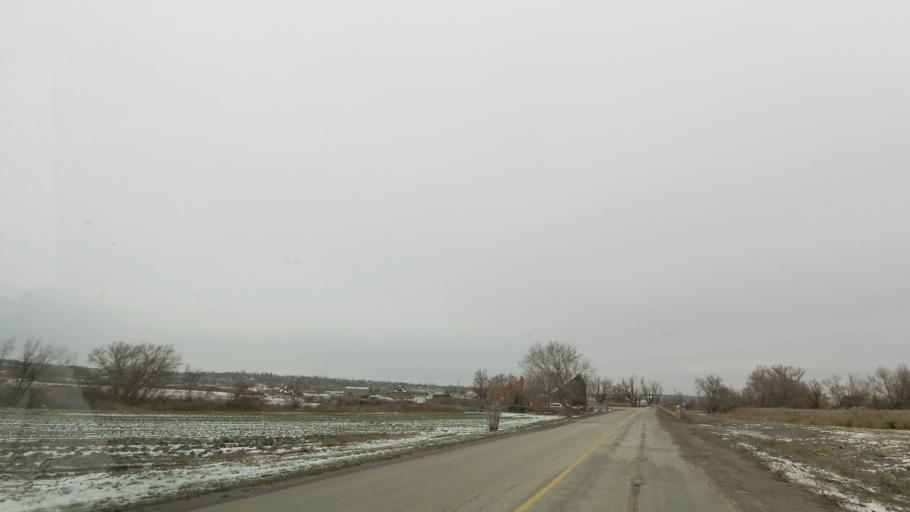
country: CA
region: Ontario
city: Bradford West Gwillimbury
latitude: 44.1093
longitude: -79.5451
